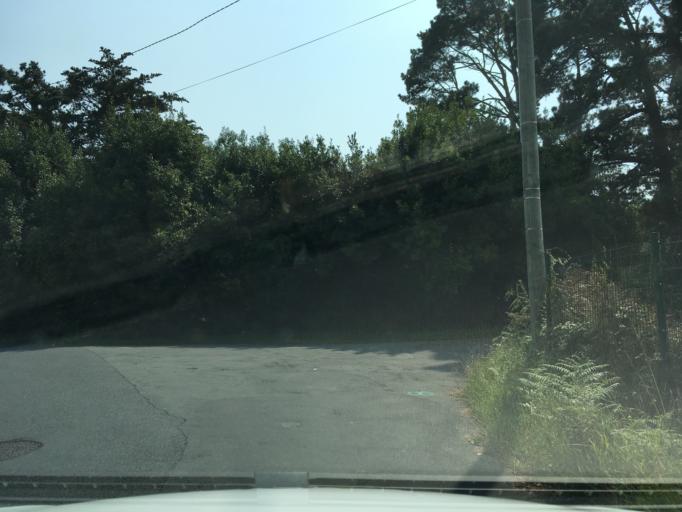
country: FR
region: Aquitaine
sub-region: Departement des Pyrenees-Atlantiques
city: Anglet
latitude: 43.5005
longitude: -1.5213
